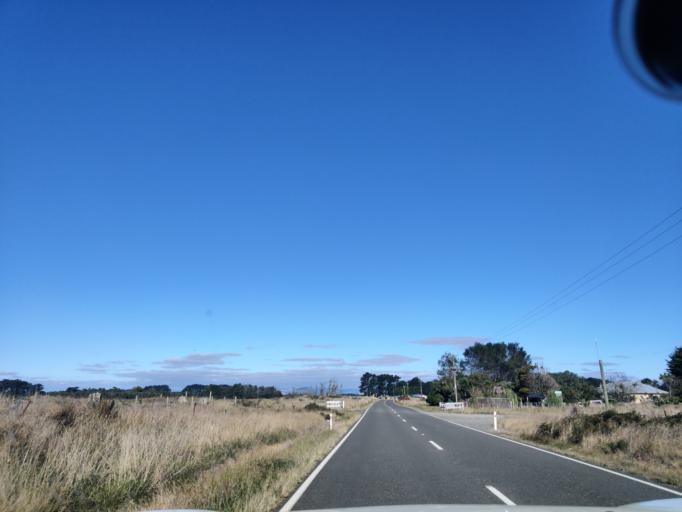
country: NZ
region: Manawatu-Wanganui
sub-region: Horowhenua District
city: Foxton
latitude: -40.3836
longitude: 175.2750
